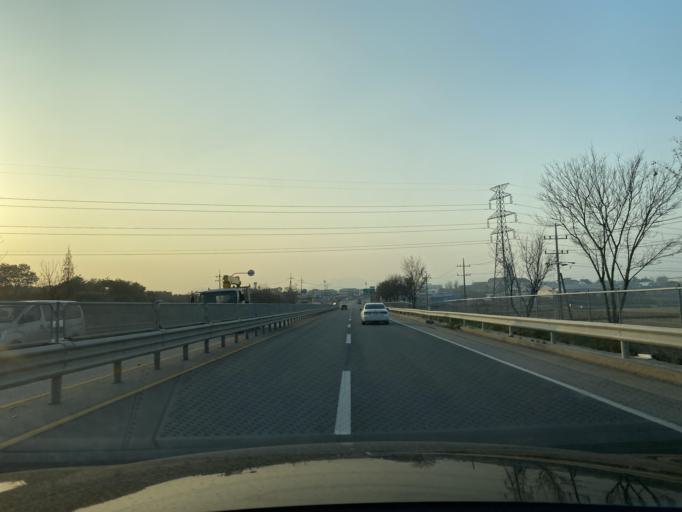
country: KR
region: Chungcheongnam-do
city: Yesan
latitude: 36.6872
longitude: 126.7625
